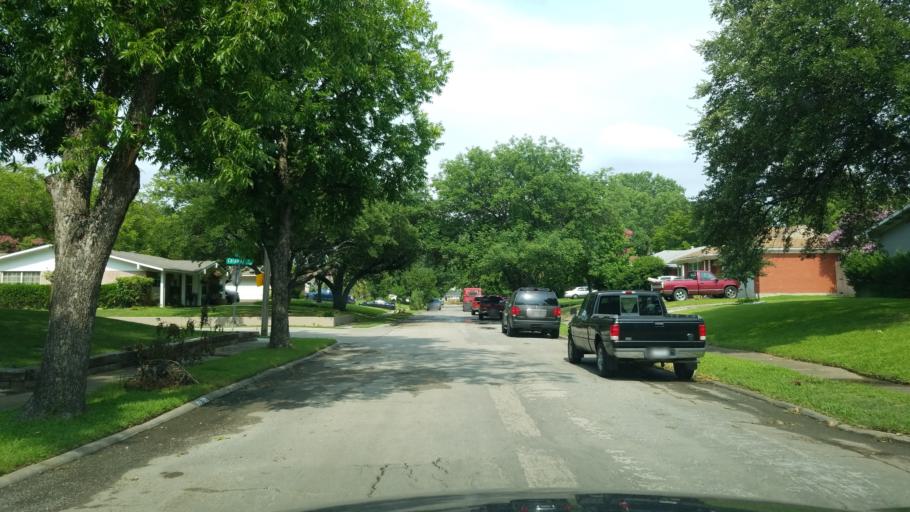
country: US
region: Texas
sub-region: Dallas County
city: Farmers Branch
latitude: 32.8970
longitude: -96.8784
